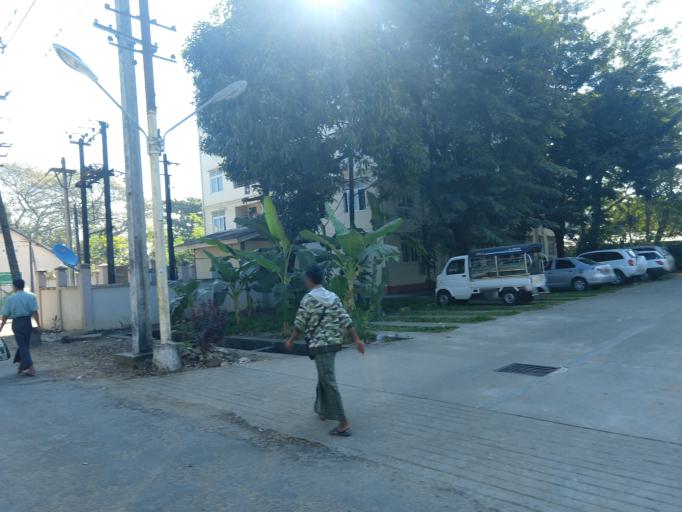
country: MM
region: Yangon
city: Yangon
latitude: 16.7902
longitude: 96.1768
